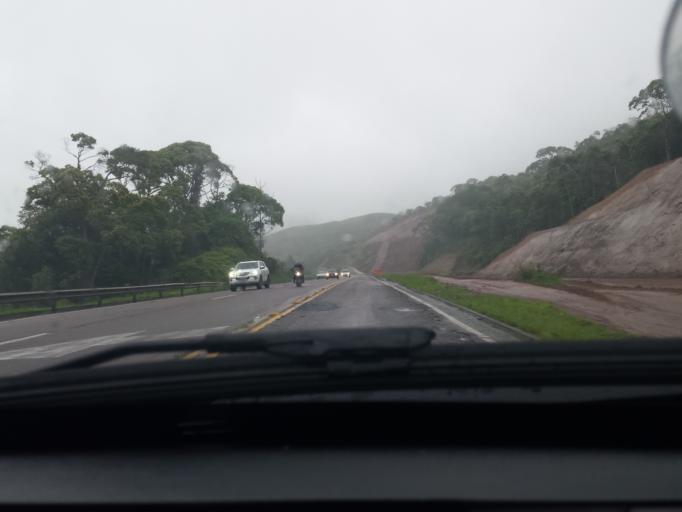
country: BR
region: Santa Catarina
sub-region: Itajai
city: Itajai
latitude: -26.8385
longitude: -48.7693
